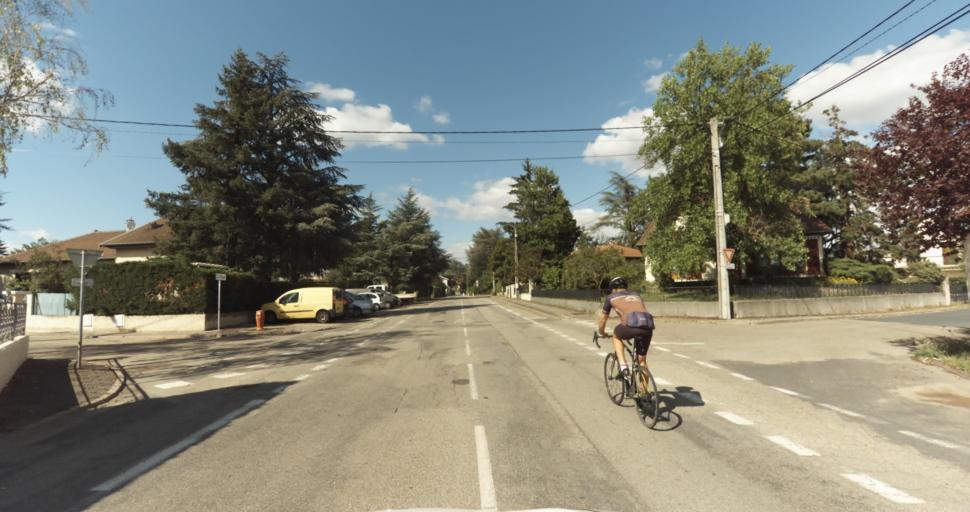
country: FR
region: Rhone-Alpes
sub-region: Departement du Rhone
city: Chaponost
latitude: 45.7125
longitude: 4.7402
